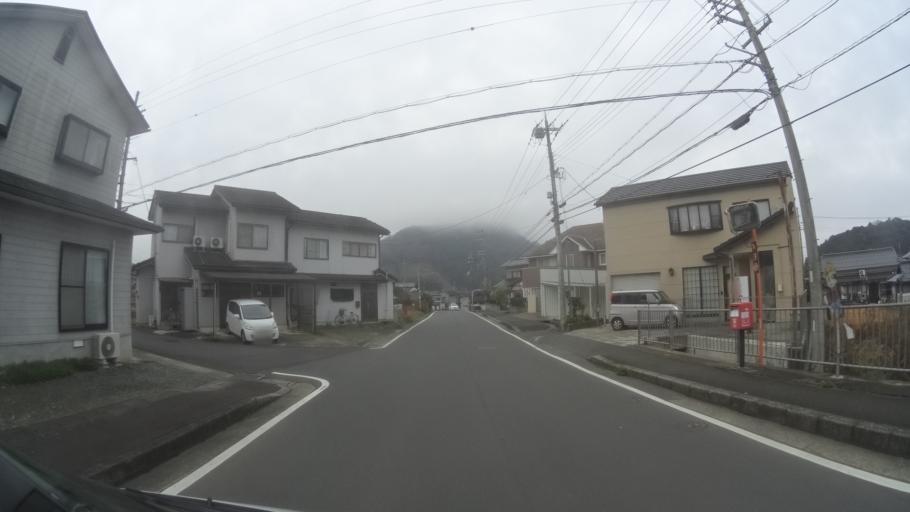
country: JP
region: Kyoto
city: Ayabe
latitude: 35.2898
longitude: 135.2631
